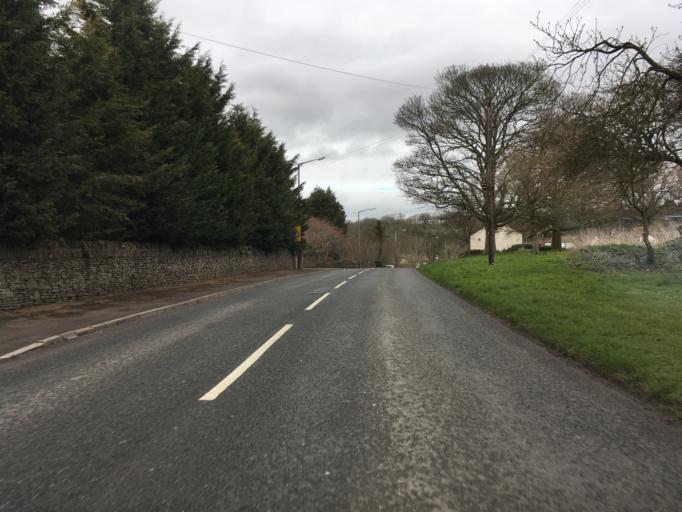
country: GB
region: England
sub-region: South Gloucestershire
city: Winterbourne
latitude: 51.5118
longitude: -2.5128
